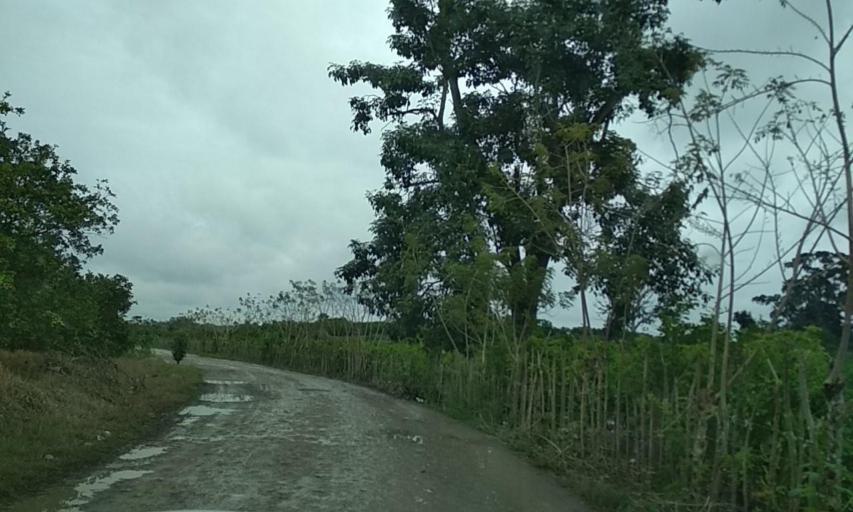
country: MX
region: Puebla
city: Espinal
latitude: 20.3039
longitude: -97.4160
